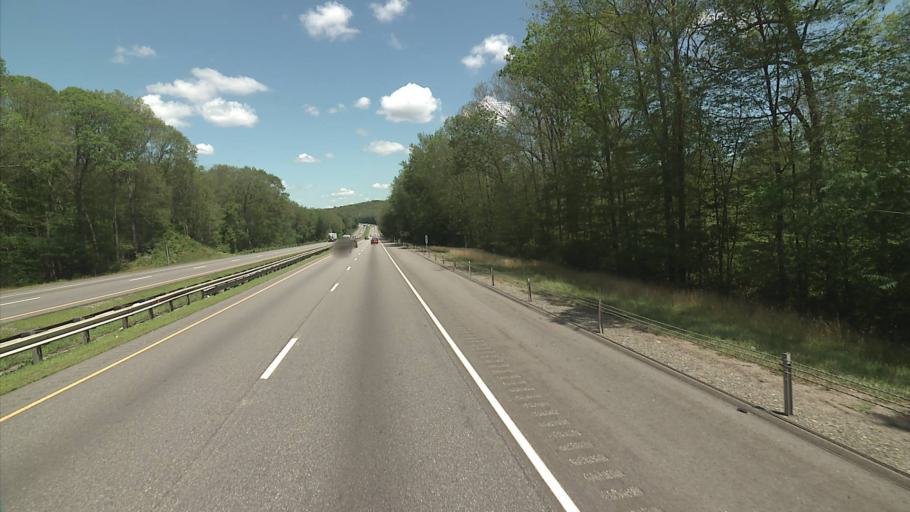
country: US
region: Connecticut
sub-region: New London County
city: Oxoboxo River
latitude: 41.4529
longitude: -72.1166
